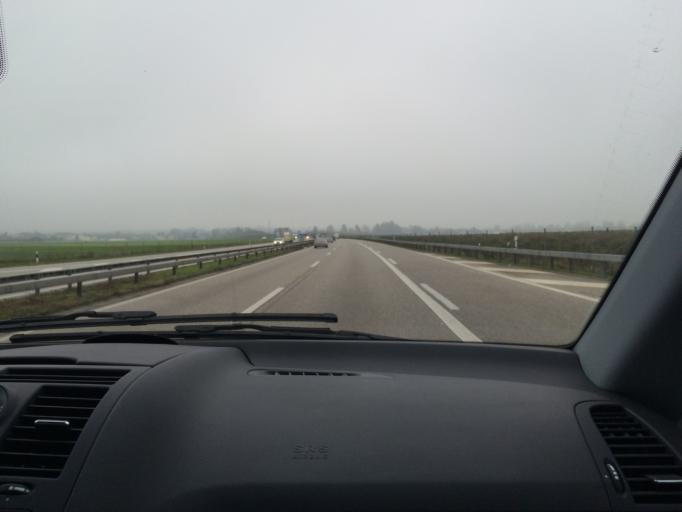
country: CH
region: Solothurn
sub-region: Bezirk Wasseramt
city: Kriegstetten
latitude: 47.1731
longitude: 7.5898
